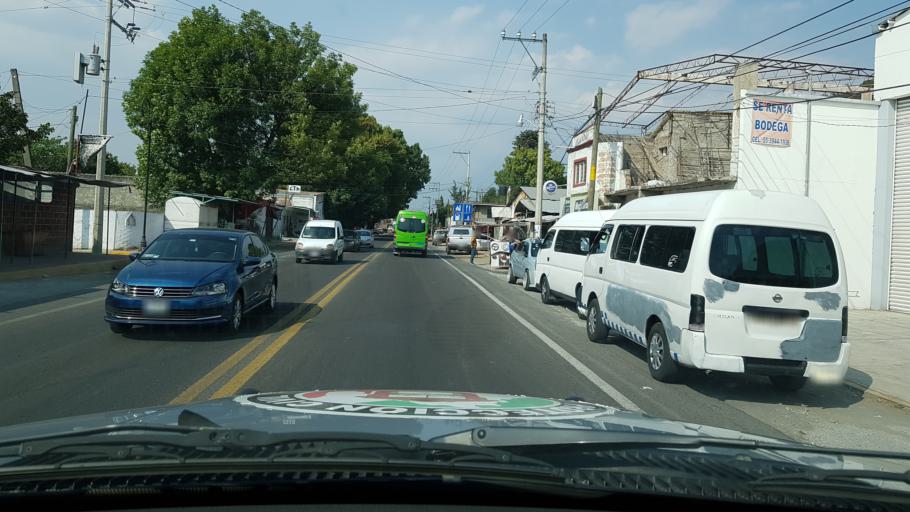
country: MX
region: Mexico
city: Tepetlixpa
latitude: 19.0278
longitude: -98.8156
